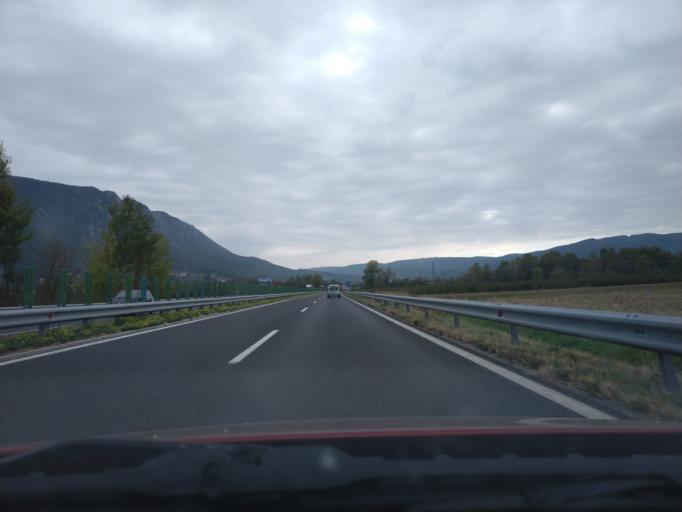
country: SI
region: Vipava
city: Vipava
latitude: 45.8496
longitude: 13.9478
